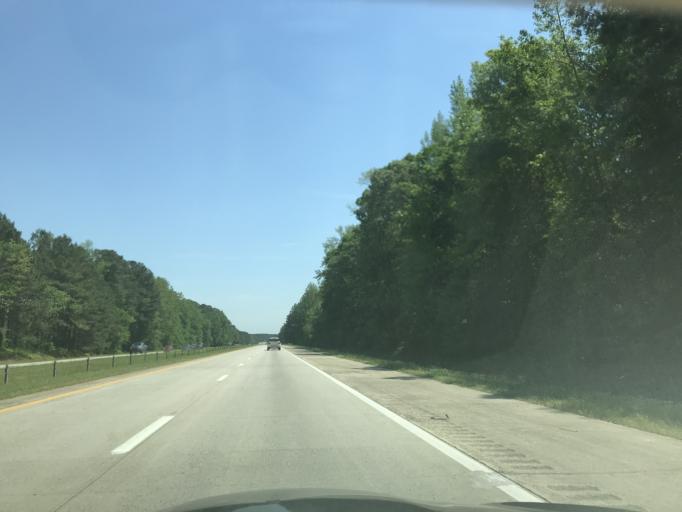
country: US
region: North Carolina
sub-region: Johnston County
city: Benson
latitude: 35.5304
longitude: -78.5680
